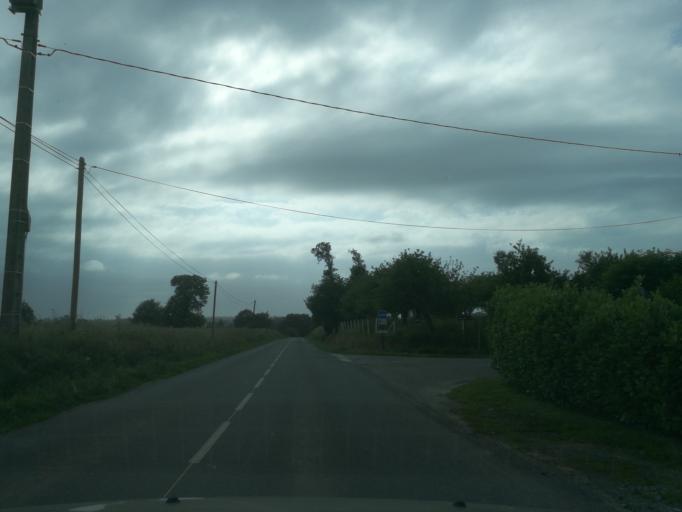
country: FR
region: Brittany
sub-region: Departement d'Ille-et-Vilaine
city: Bedee
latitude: 48.2048
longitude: -1.9609
